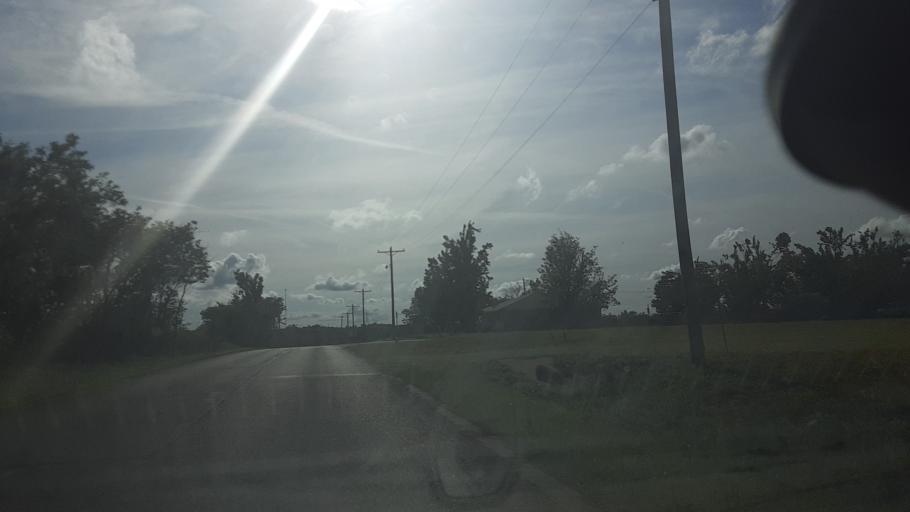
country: US
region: Oklahoma
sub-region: Logan County
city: Guthrie
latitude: 36.0576
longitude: -97.4055
